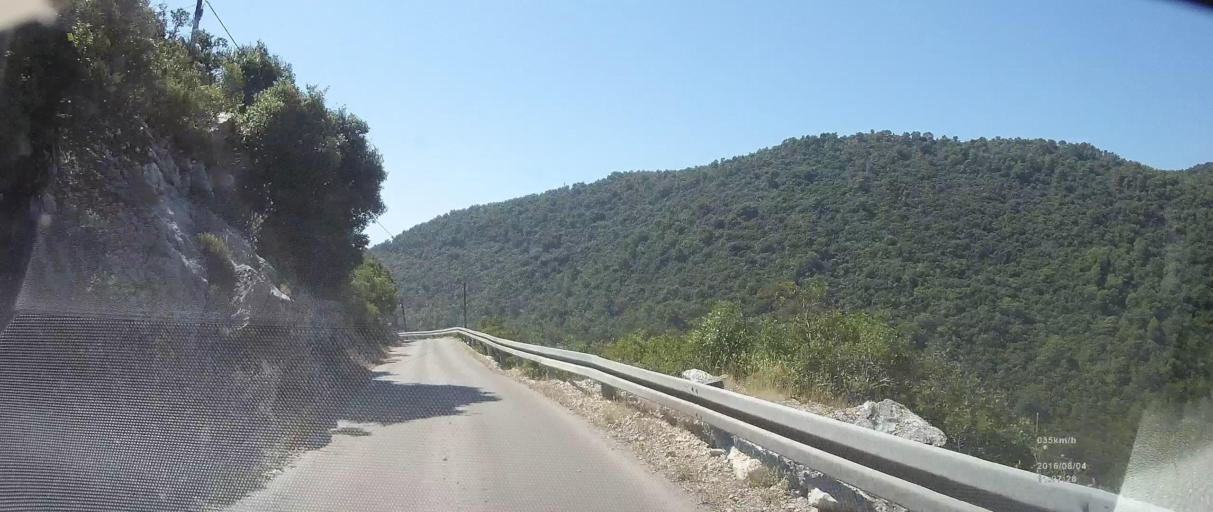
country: HR
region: Dubrovacko-Neretvanska
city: Blato
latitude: 42.7675
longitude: 17.4666
